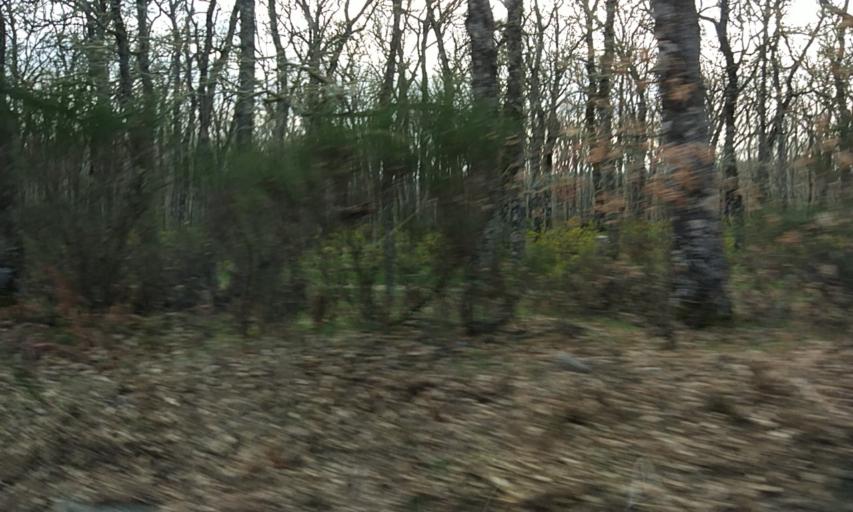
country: ES
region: Castille and Leon
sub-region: Provincia de Salamanca
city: Villasrubias
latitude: 40.3315
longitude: -6.6450
